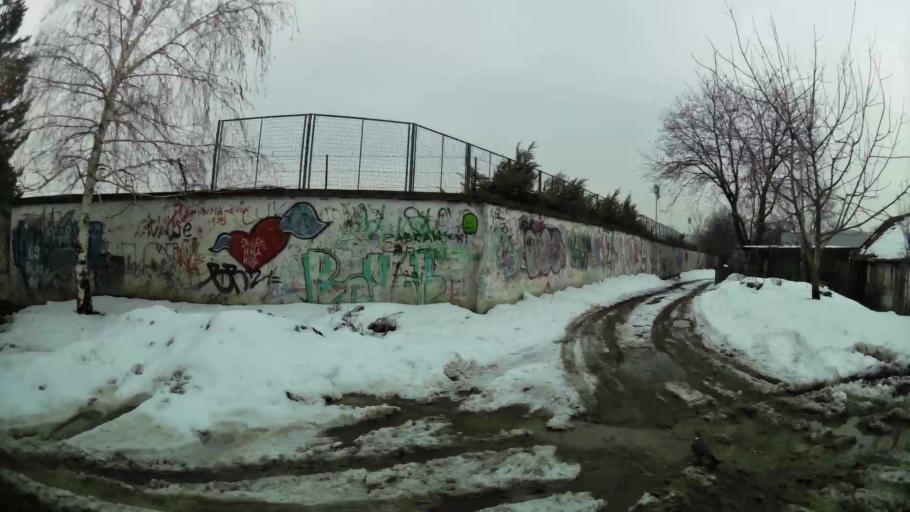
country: RS
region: Central Serbia
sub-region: Belgrade
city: Zemun
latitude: 44.8537
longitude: 20.3803
